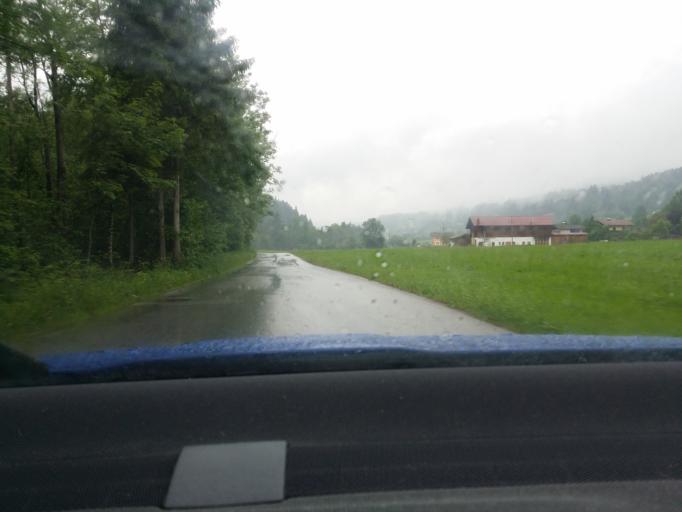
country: AT
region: Salzburg
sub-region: Politischer Bezirk Hallein
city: Abtenau
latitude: 47.5901
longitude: 13.3368
